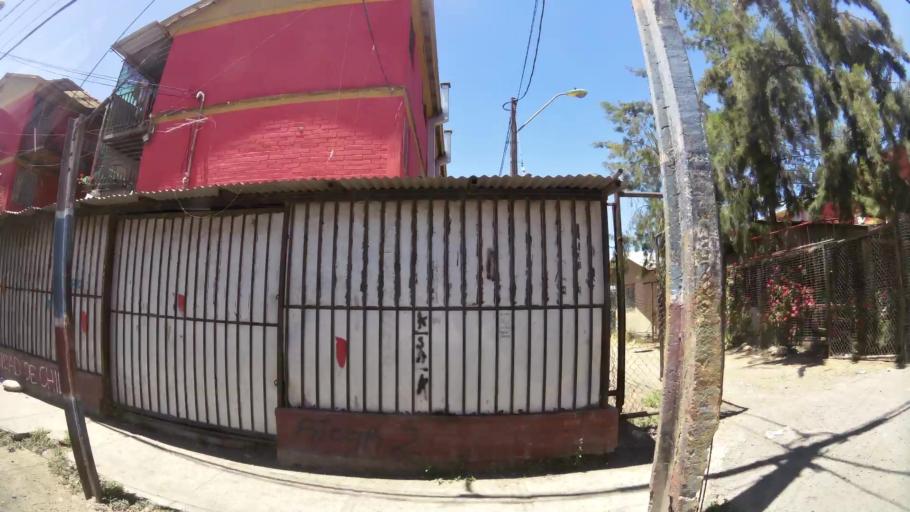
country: CL
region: Santiago Metropolitan
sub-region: Provincia de Maipo
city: San Bernardo
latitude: -33.5778
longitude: -70.6713
